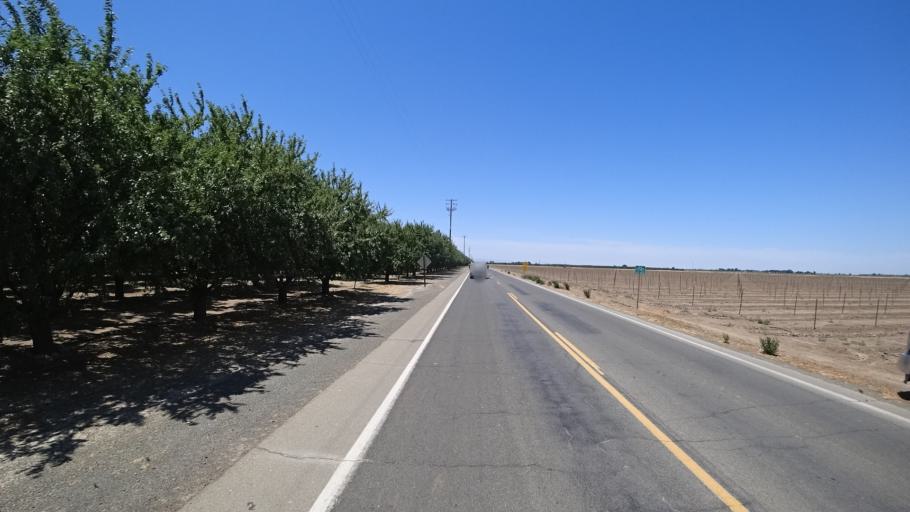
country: US
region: California
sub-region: Kings County
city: Armona
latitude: 36.3426
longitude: -119.7467
